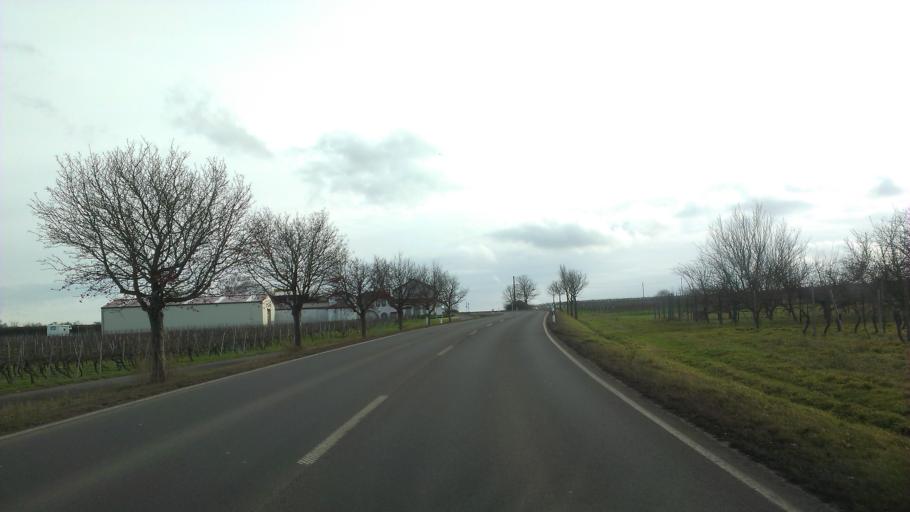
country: DE
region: Rheinland-Pfalz
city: Hackenheim
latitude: 49.8291
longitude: 7.8872
